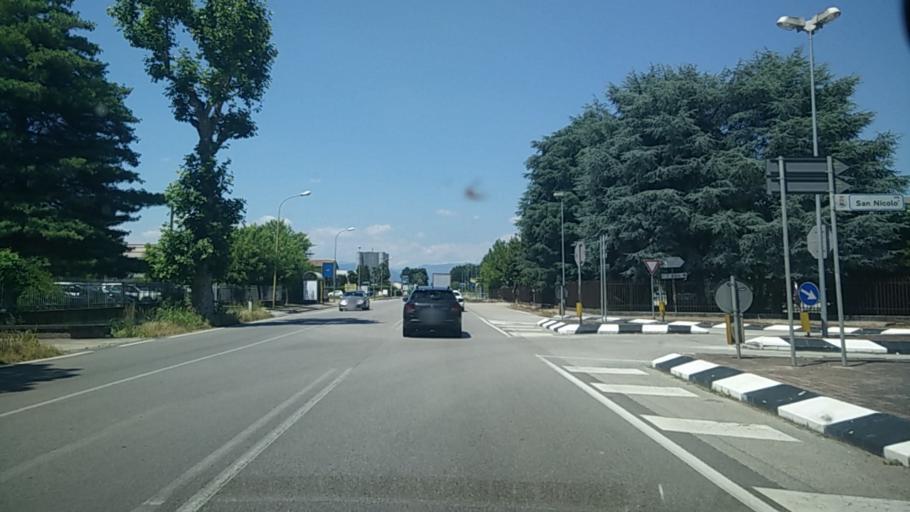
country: IT
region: Veneto
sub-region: Provincia di Padova
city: San Giorgio in Bosco
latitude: 45.6001
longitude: 11.8028
